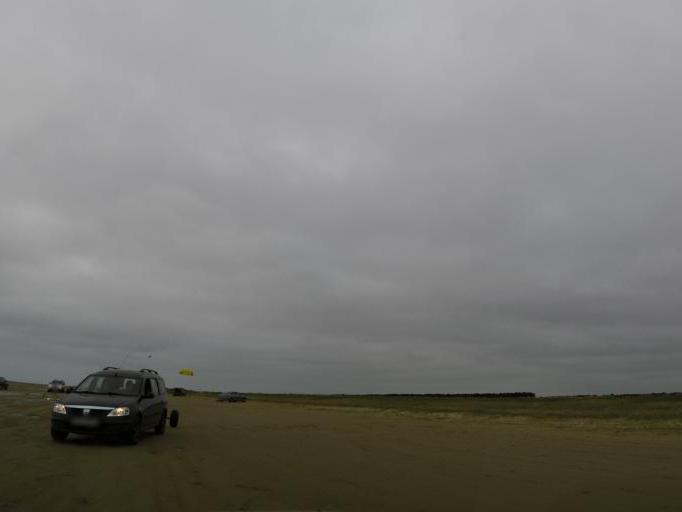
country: DE
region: Schleswig-Holstein
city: List
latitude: 55.0856
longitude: 8.5100
